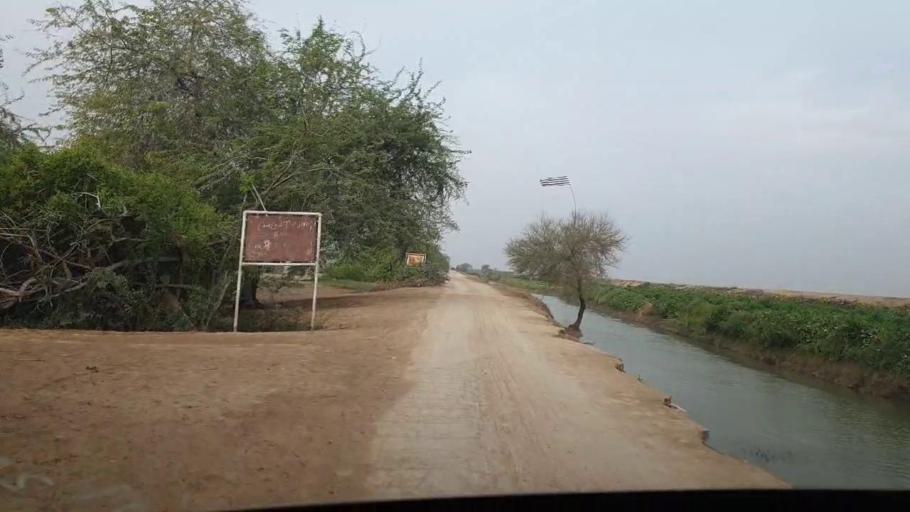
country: PK
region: Sindh
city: Chuhar Jamali
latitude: 24.3999
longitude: 67.9667
